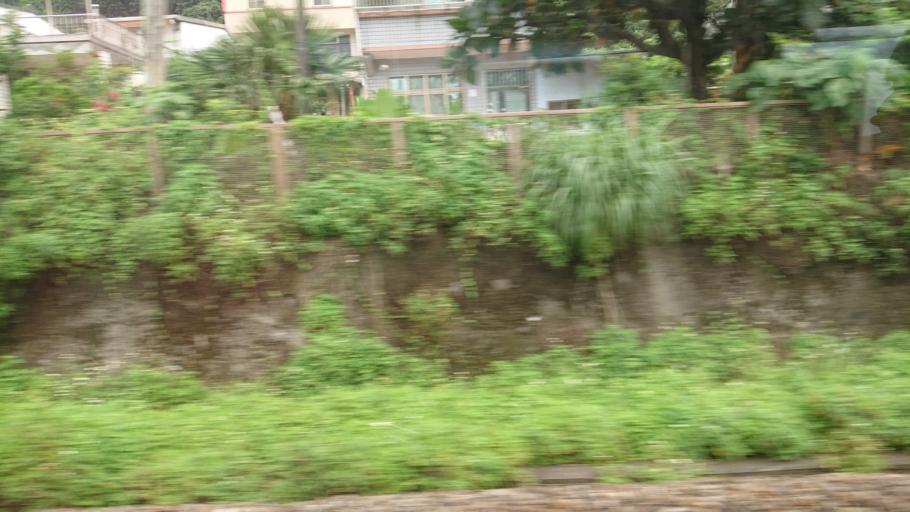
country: TW
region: Taiwan
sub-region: Yilan
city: Yilan
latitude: 24.9366
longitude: 121.8872
